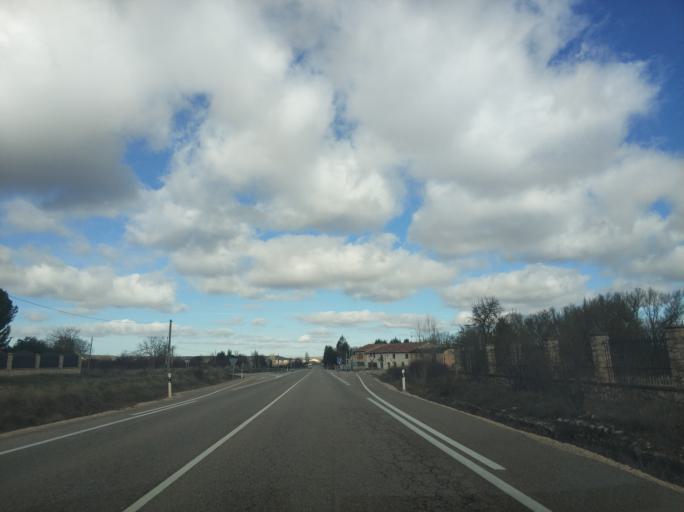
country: ES
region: Castille and Leon
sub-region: Provincia de Burgos
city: Revillarruz
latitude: 42.2288
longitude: -3.6595
